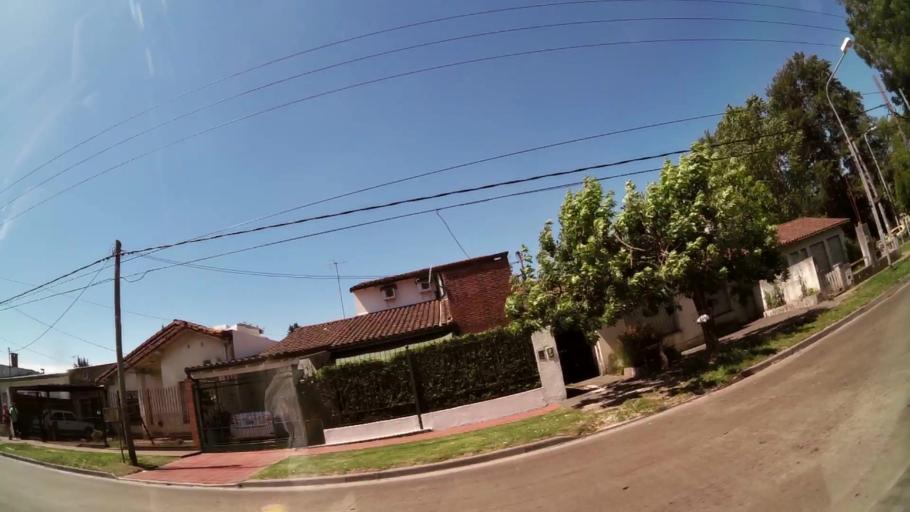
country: AR
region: Buenos Aires
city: Hurlingham
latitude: -34.4953
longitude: -58.6537
